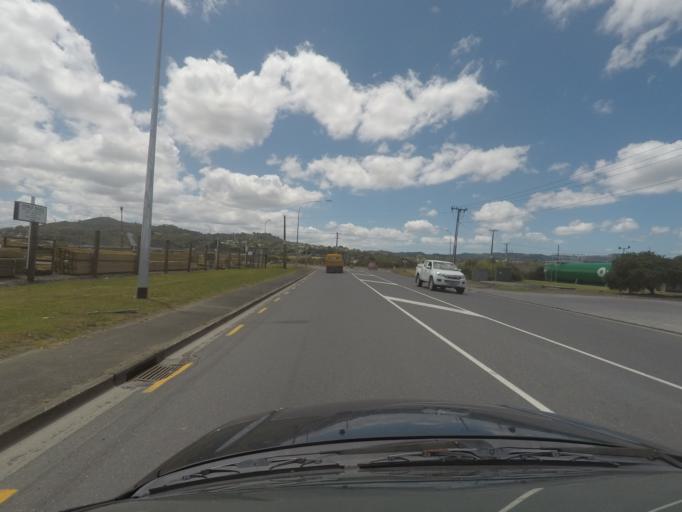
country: NZ
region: Northland
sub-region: Whangarei
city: Whangarei
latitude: -35.7395
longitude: 174.3342
